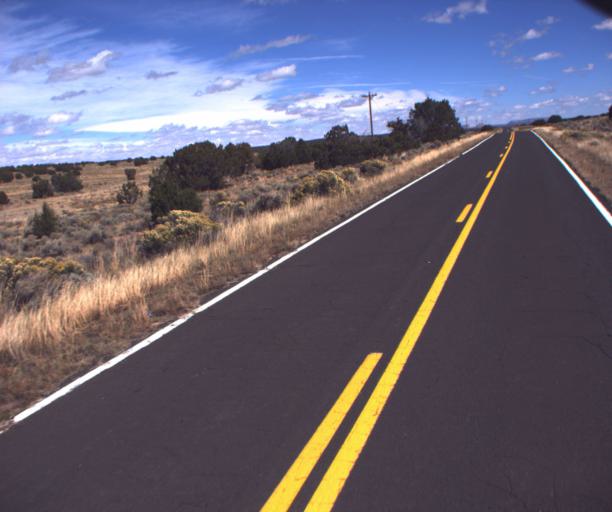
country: US
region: New Mexico
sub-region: McKinley County
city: Zuni Pueblo
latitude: 34.9955
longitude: -109.0962
